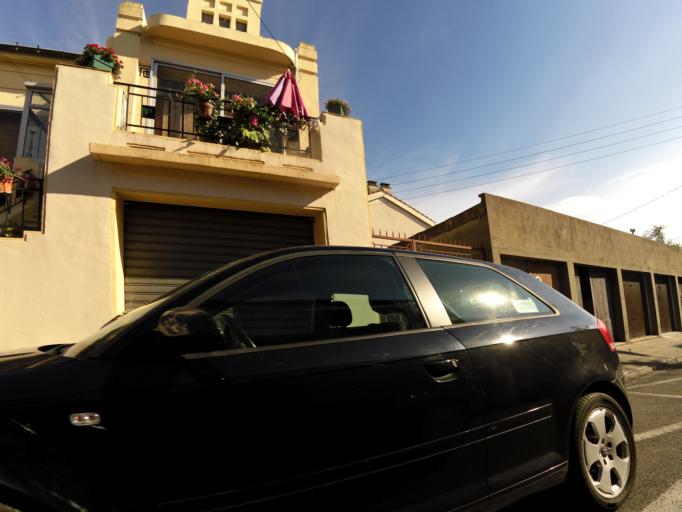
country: FR
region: Languedoc-Roussillon
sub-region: Departement du Gard
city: Nimes
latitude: 43.8495
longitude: 4.3671
